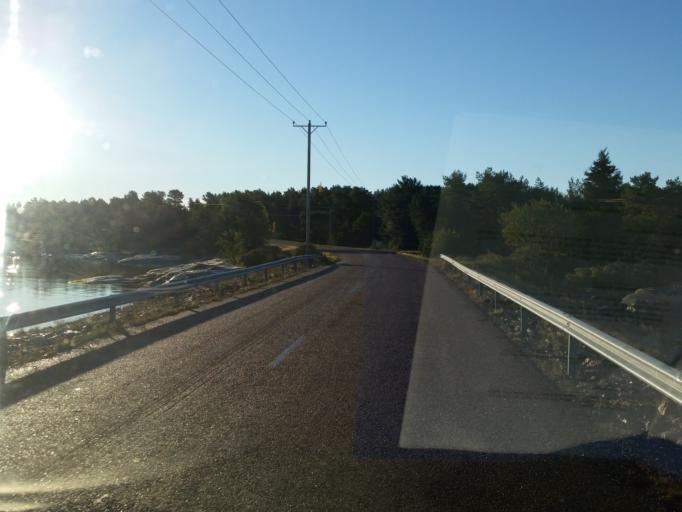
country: AX
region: Alands skaergard
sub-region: Vardoe
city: Vardoe
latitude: 60.3105
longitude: 20.3755
